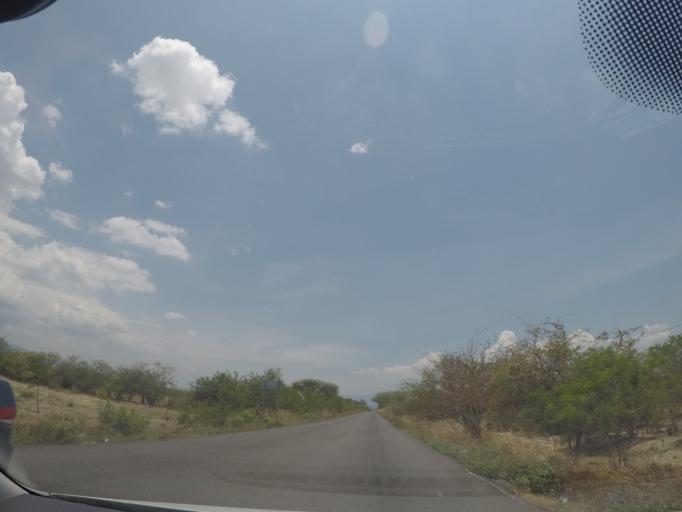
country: MX
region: Oaxaca
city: Santa Maria Jalapa del Marques
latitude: 16.4398
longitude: -95.4699
